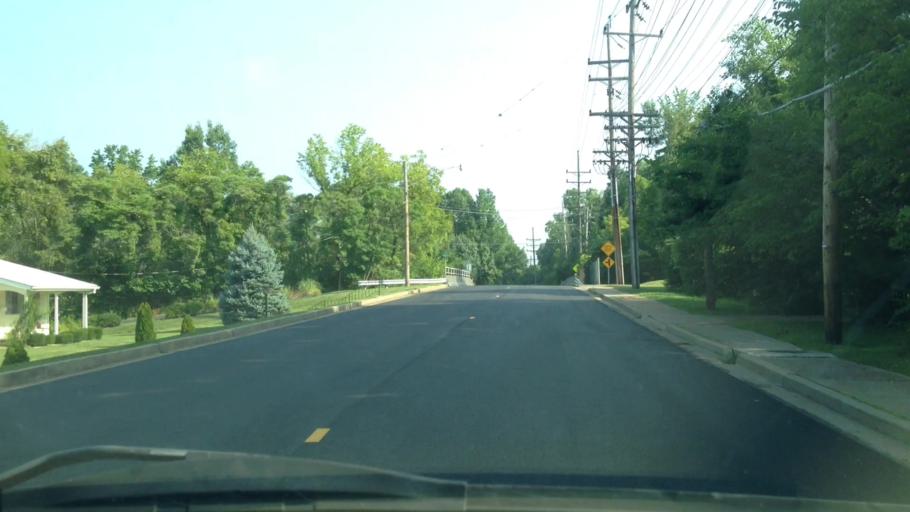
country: US
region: Missouri
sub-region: Saint Louis County
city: Des Peres
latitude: 38.5757
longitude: -90.4348
